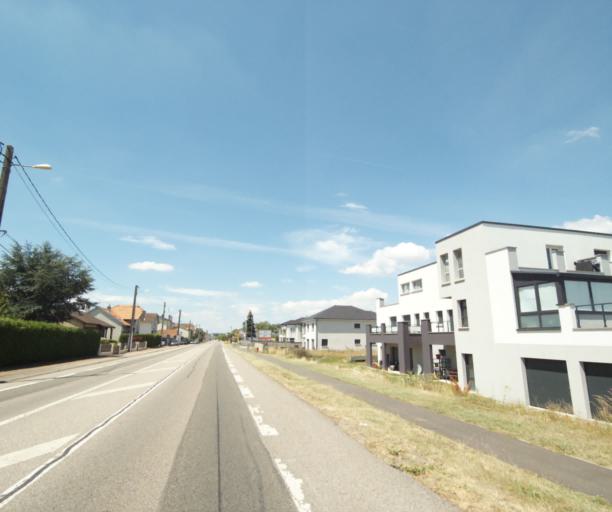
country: FR
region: Lorraine
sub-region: Departement de Meurthe-et-Moselle
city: Chanteheux
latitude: 48.5917
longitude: 6.5234
